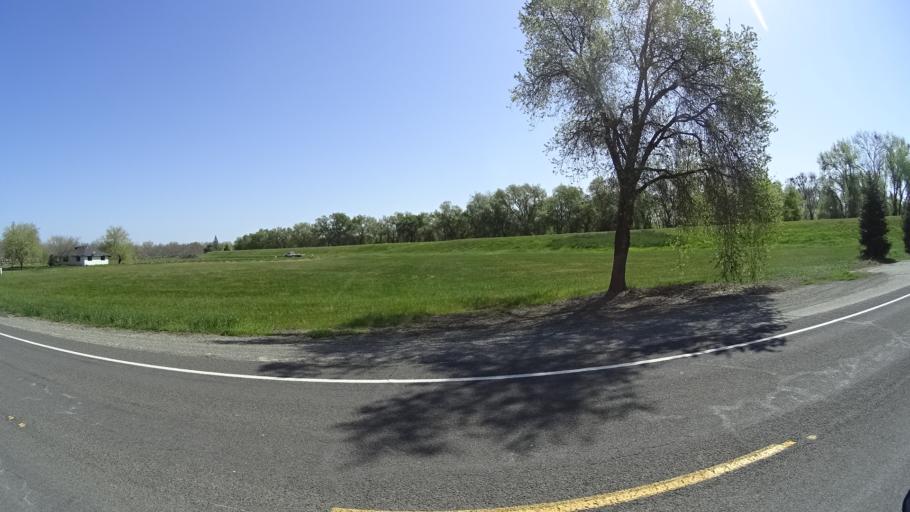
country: US
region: California
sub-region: Glenn County
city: Willows
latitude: 39.4540
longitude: -122.0174
